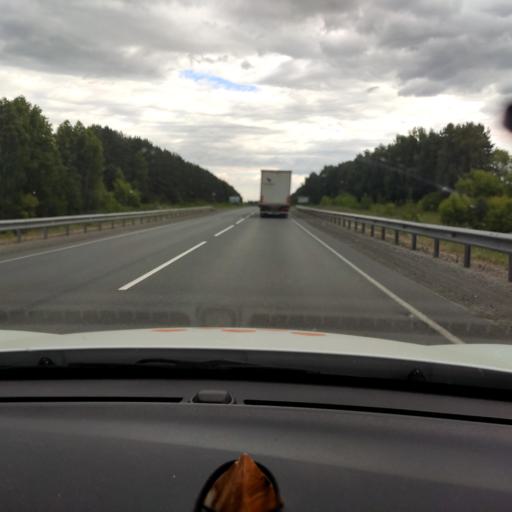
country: RU
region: Mariy-El
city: Pomary
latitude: 55.9367
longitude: 48.3719
